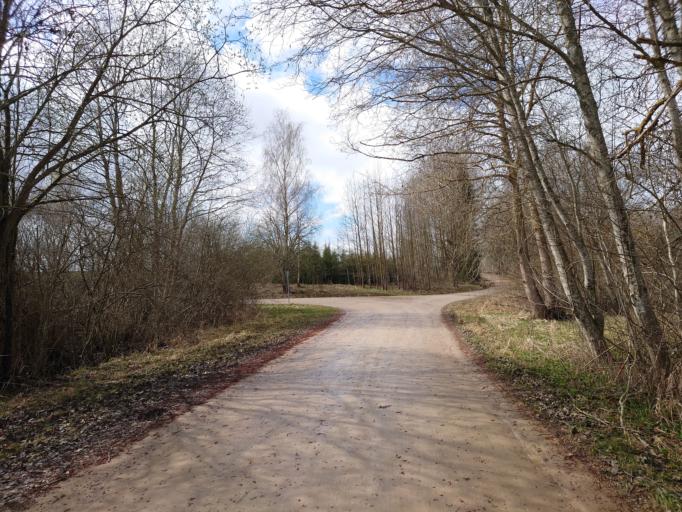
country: EE
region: Vorumaa
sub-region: Voru linn
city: Voru
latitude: 57.9065
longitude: 26.9752
